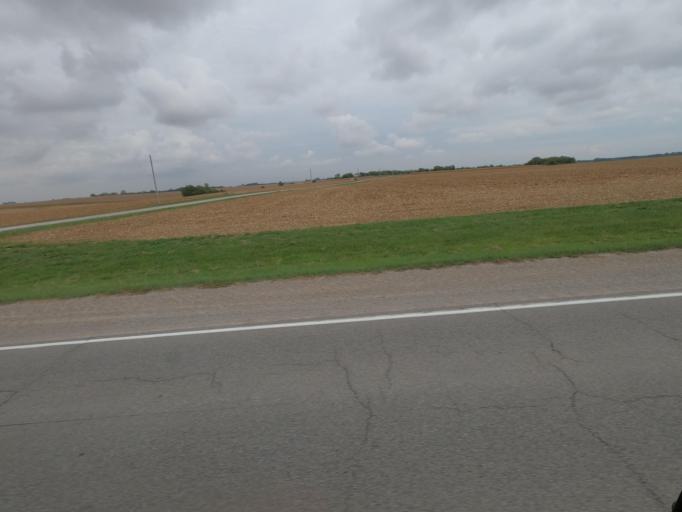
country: US
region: Iowa
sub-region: Wapello County
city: Ottumwa
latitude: 40.9707
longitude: -92.2365
